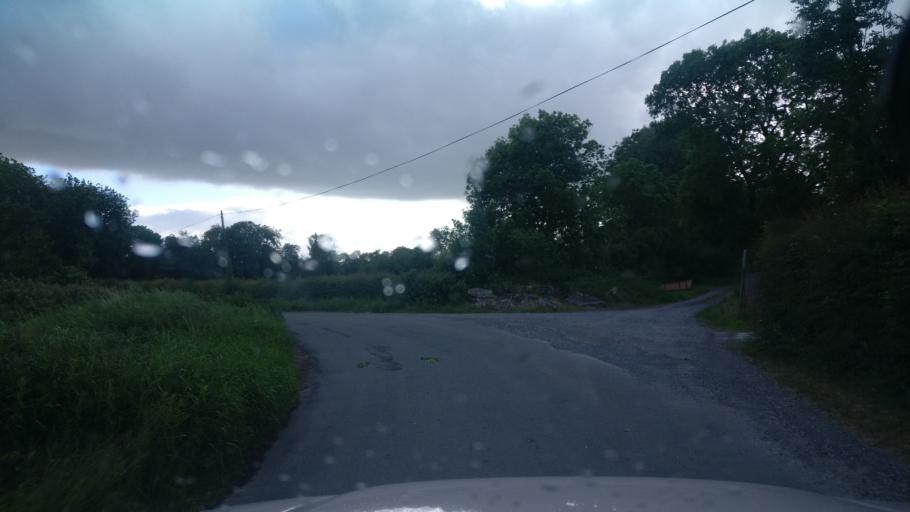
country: IE
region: Connaught
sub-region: County Galway
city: Ballinasloe
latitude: 53.2335
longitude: -8.2091
